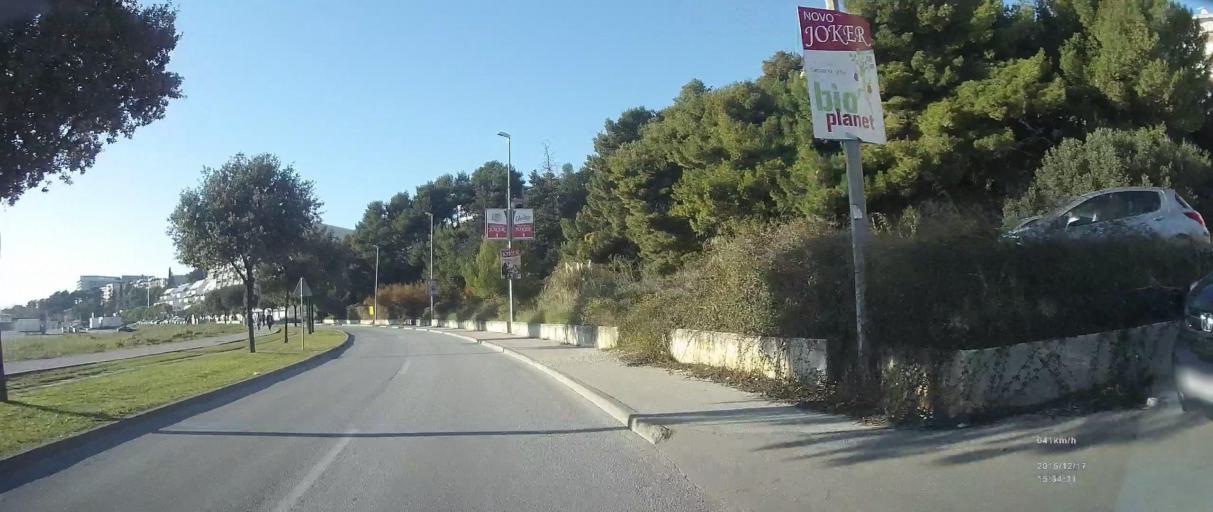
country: HR
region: Splitsko-Dalmatinska
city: Vranjic
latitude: 43.5033
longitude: 16.4795
